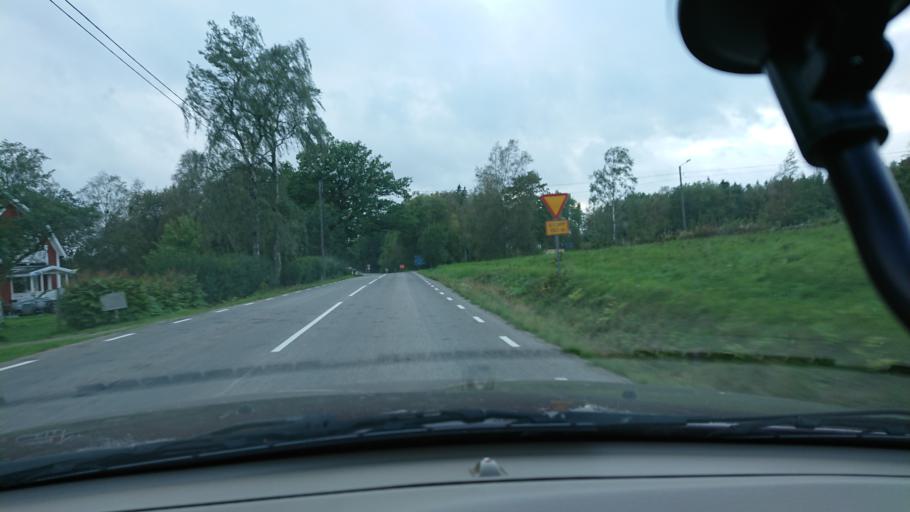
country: SE
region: Kronoberg
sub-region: Vaxjo Kommun
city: Lammhult
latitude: 57.0894
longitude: 14.6438
